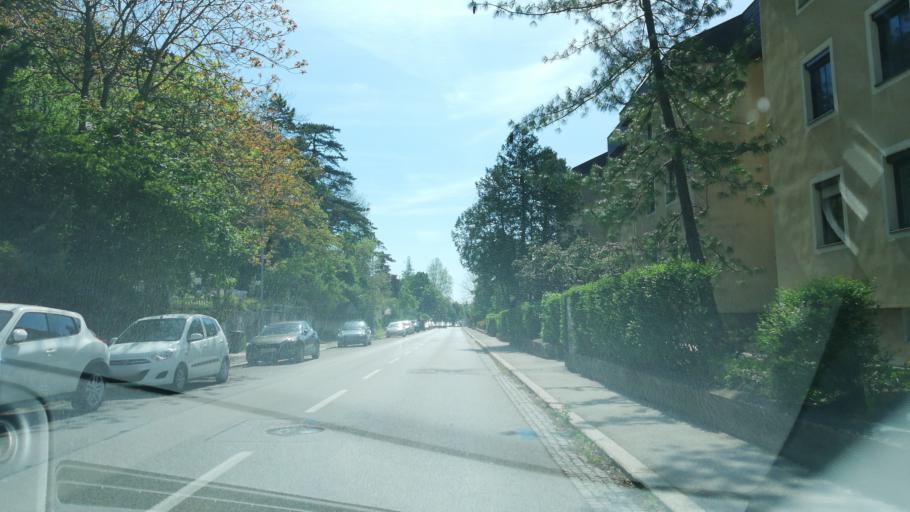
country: AT
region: Lower Austria
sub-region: Politischer Bezirk Baden
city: Baden
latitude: 48.0144
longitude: 16.1999
